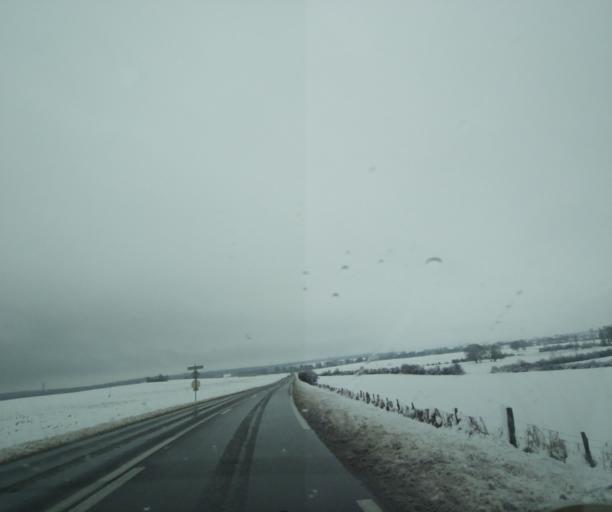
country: FR
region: Champagne-Ardenne
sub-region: Departement de la Haute-Marne
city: Montier-en-Der
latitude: 48.5175
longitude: 4.8089
